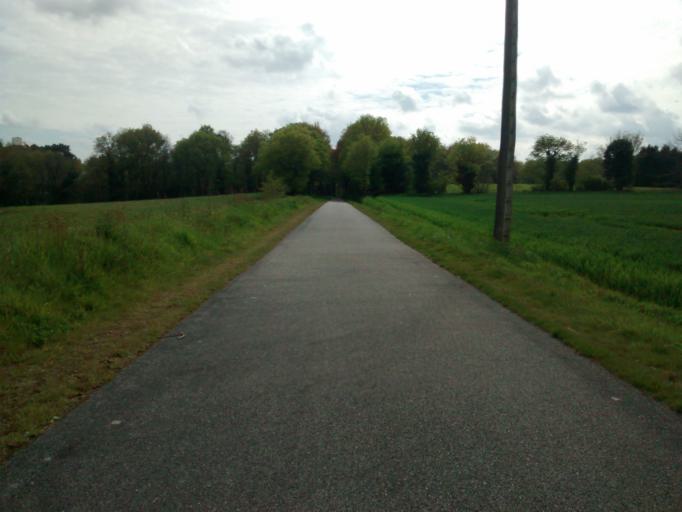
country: FR
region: Brittany
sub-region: Departement du Morbihan
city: Malestroit
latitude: 47.7963
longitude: -2.4017
